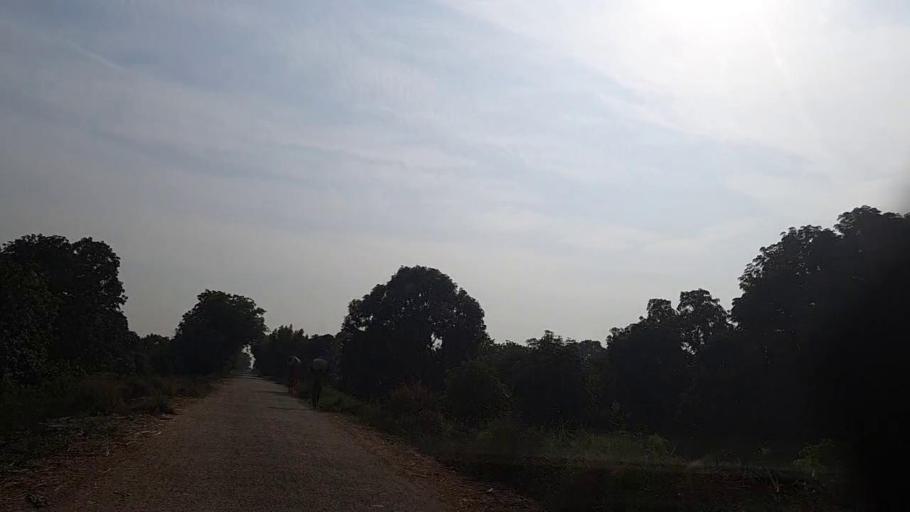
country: PK
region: Sindh
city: Daur
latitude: 26.4023
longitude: 68.2133
